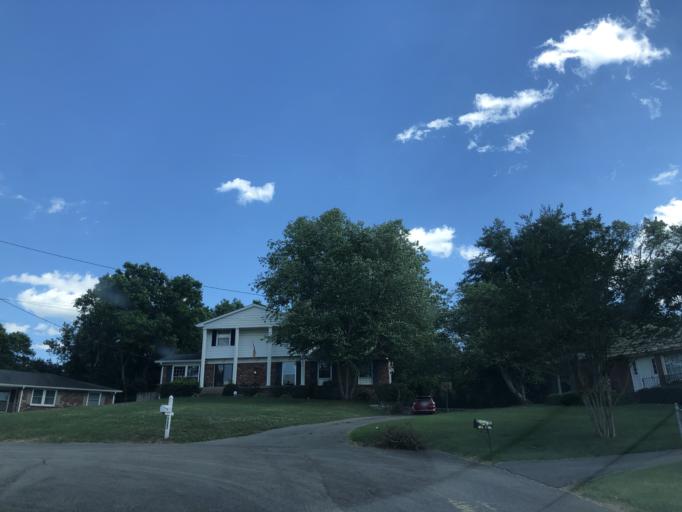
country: US
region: Tennessee
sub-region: Davidson County
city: Belle Meade
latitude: 36.0595
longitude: -86.9344
